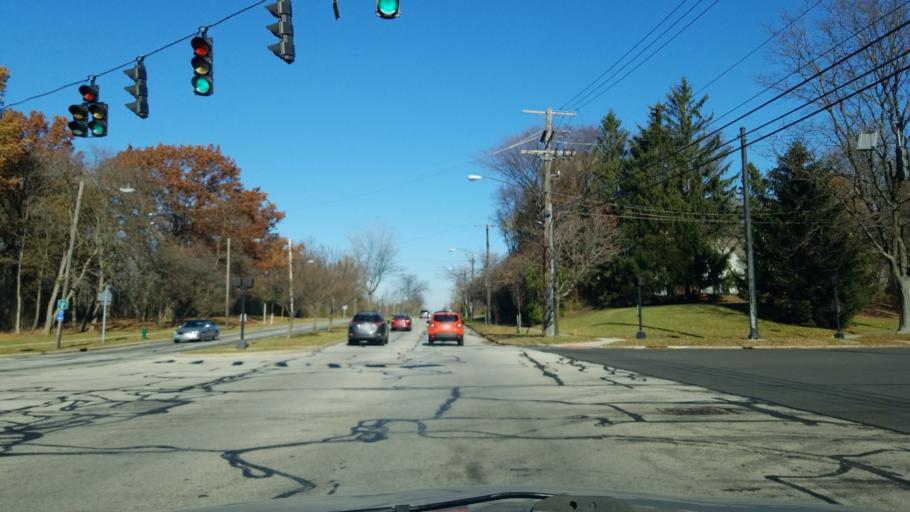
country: US
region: Ohio
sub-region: Cuyahoga County
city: Shaker Heights
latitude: 41.4794
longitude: -81.5362
